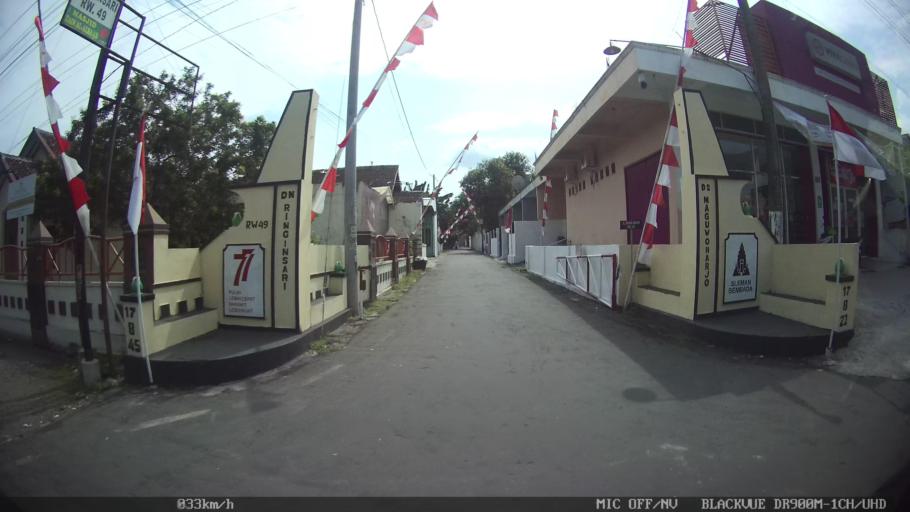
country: ID
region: Daerah Istimewa Yogyakarta
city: Depok
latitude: -7.7742
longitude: 110.4358
